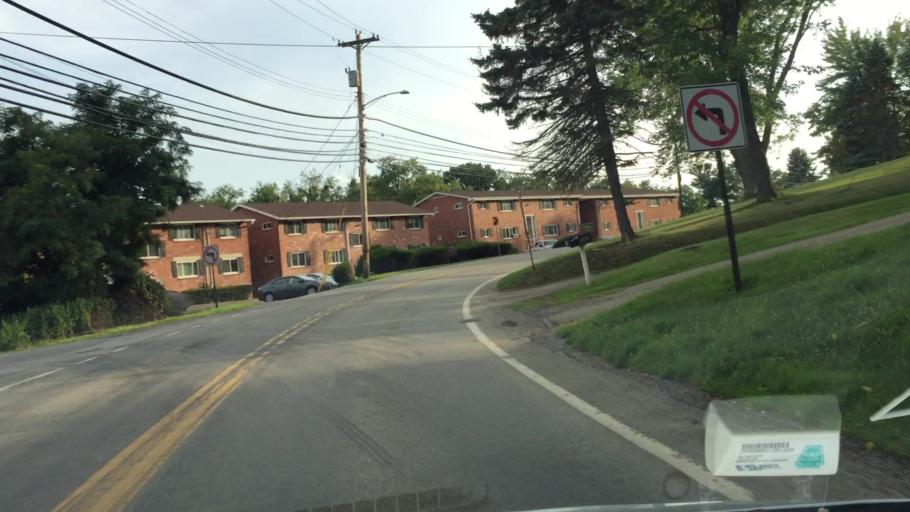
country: US
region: Pennsylvania
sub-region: Allegheny County
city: Carnot-Moon
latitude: 40.5110
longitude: -80.2340
